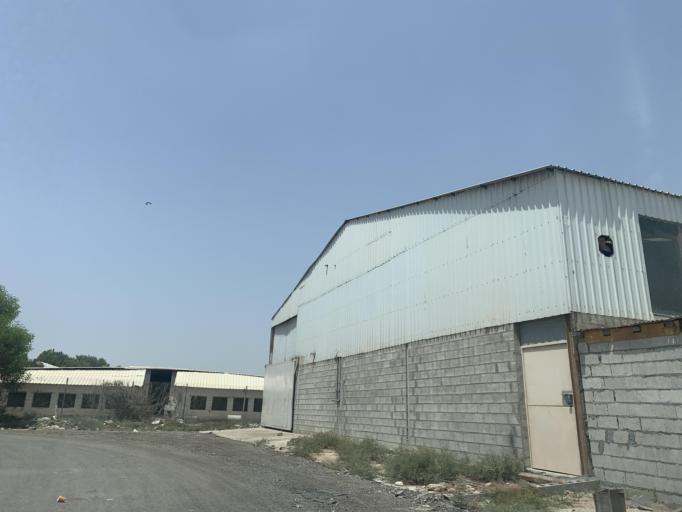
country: BH
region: Central Governorate
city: Madinat Hamad
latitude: 26.1547
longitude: 50.4939
